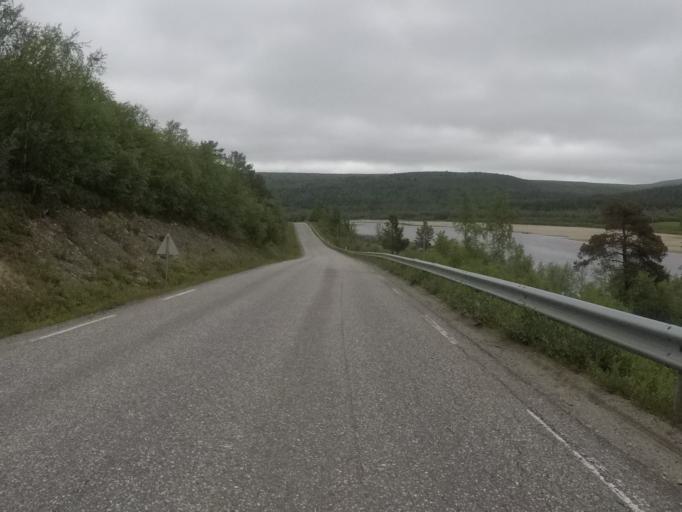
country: NO
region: Finnmark Fylke
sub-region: Karasjok
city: Karasjohka
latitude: 69.5159
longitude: 25.8624
